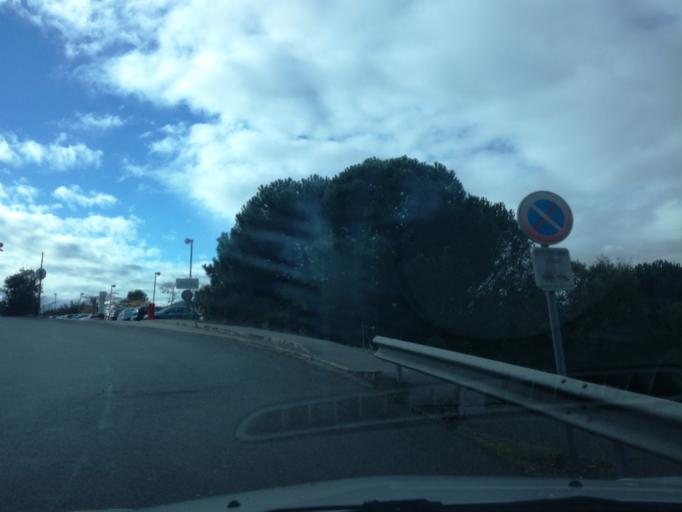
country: FR
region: Provence-Alpes-Cote d'Azur
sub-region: Departement des Alpes-Maritimes
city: Pegomas
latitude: 43.6211
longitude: 6.9324
